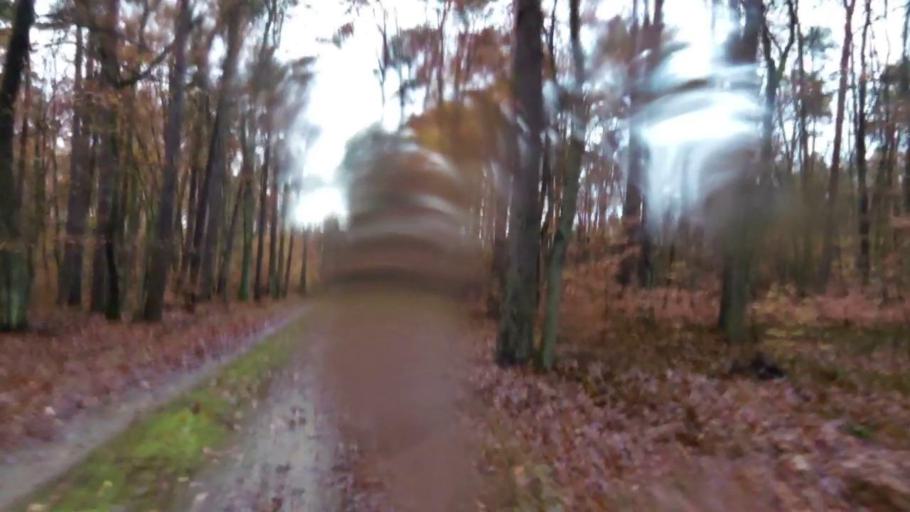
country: PL
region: West Pomeranian Voivodeship
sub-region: Powiat goleniowski
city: Stepnica
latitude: 53.6508
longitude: 14.6955
